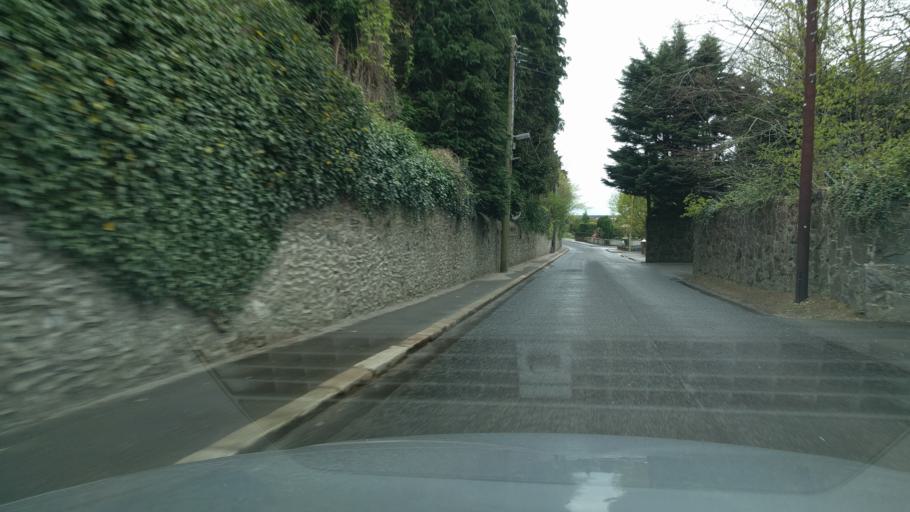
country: GB
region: Northern Ireland
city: Rostrevor
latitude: 54.1048
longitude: -6.2021
